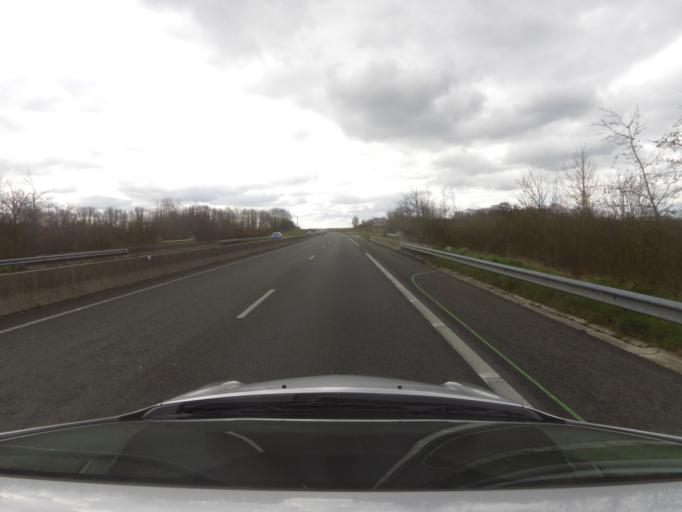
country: FR
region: Nord-Pas-de-Calais
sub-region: Departement du Pas-de-Calais
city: Saint-Josse
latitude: 50.4417
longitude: 1.6928
